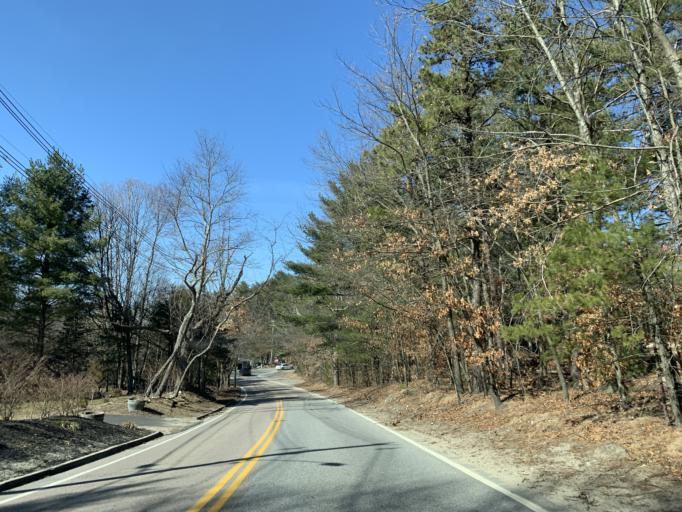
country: US
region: Massachusetts
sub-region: Norfolk County
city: Sharon
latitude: 42.1472
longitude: -71.1776
